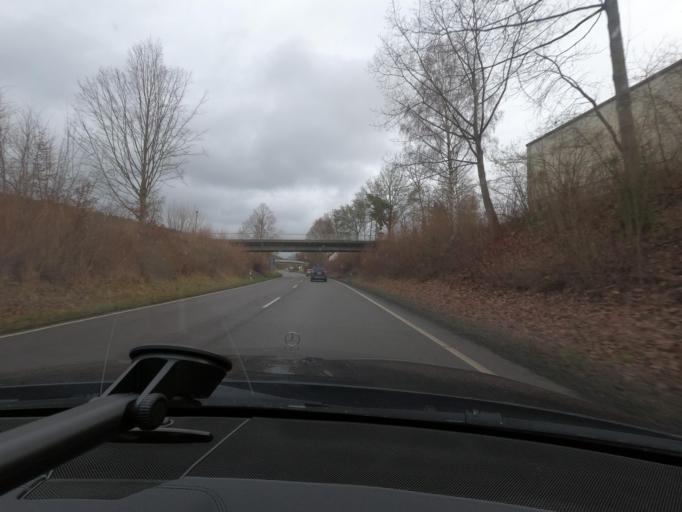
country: DE
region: Hesse
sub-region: Regierungsbezirk Kassel
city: Wolfhagen
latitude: 51.3246
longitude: 9.1791
